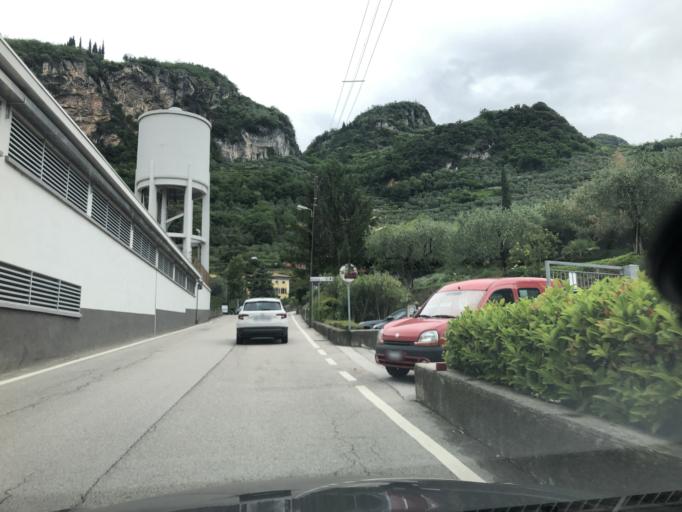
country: IT
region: Trentino-Alto Adige
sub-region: Provincia di Trento
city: Tenno
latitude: 45.9103
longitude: 10.8389
